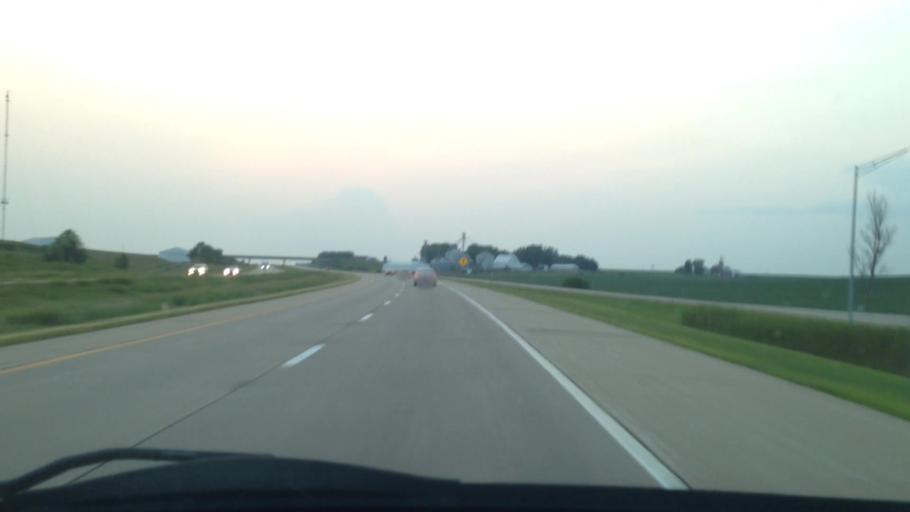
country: US
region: Iowa
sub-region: Buchanan County
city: Jesup
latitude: 42.3288
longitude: -91.9983
